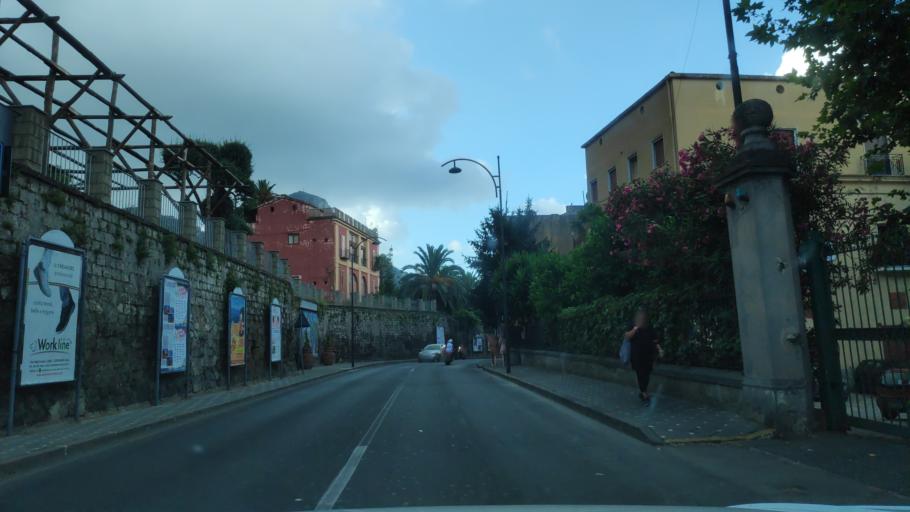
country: IT
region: Campania
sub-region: Provincia di Napoli
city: Meta
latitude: 40.6408
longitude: 14.4187
